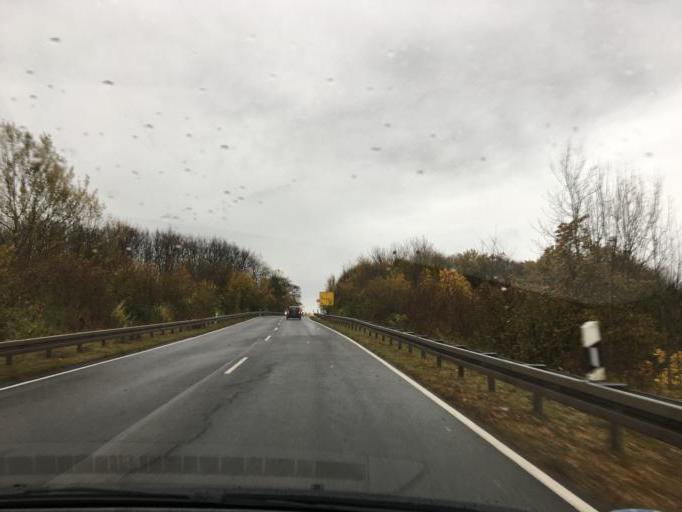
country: DE
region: North Rhine-Westphalia
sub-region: Regierungsbezirk Koln
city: Vettweiss
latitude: 50.6767
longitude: 6.5705
